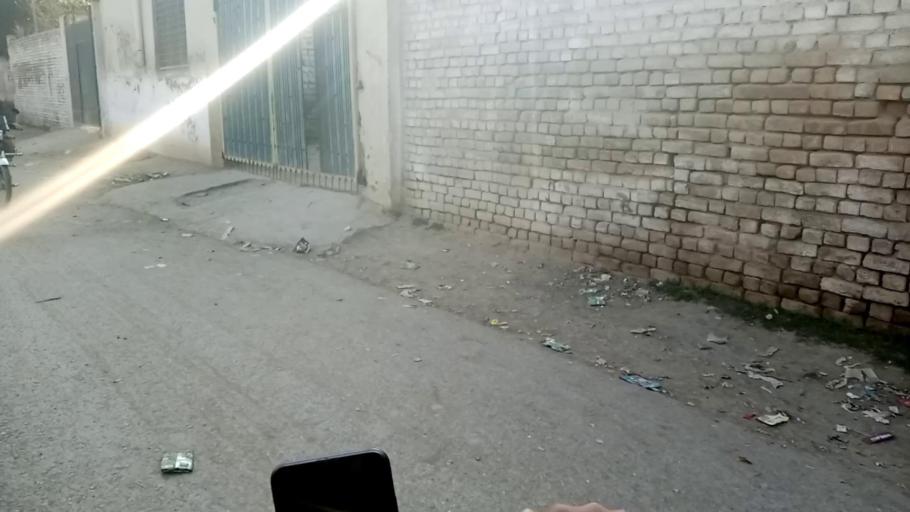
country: PK
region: Khyber Pakhtunkhwa
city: Peshawar
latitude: 34.0074
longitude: 71.4686
